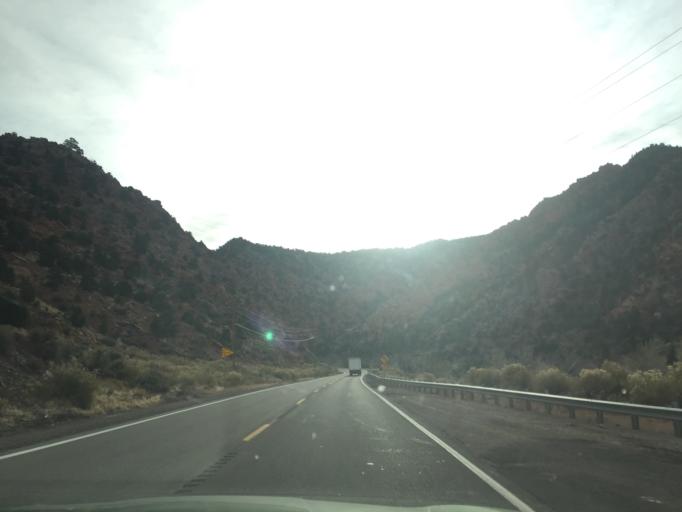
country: US
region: Utah
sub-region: Iron County
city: Cedar City
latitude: 37.6728
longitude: -113.0431
